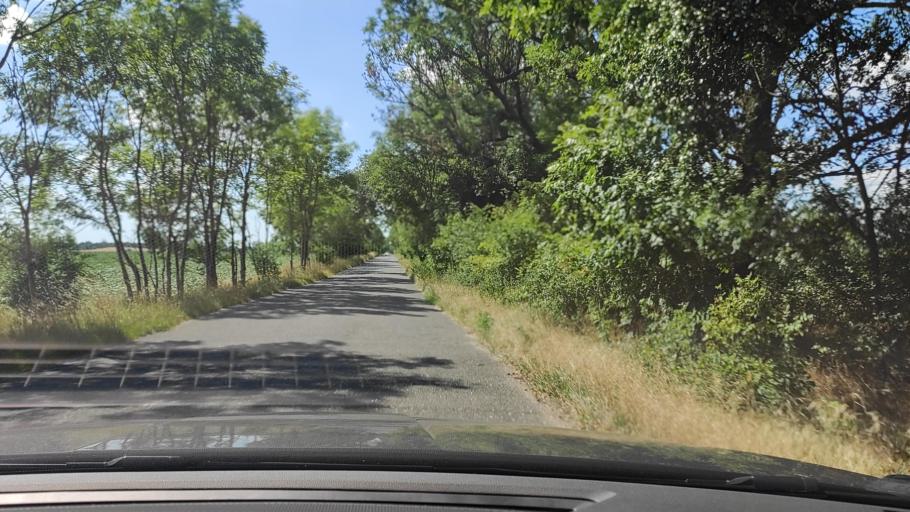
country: PL
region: Greater Poland Voivodeship
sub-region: Powiat poznanski
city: Kobylnica
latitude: 52.4963
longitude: 17.1228
